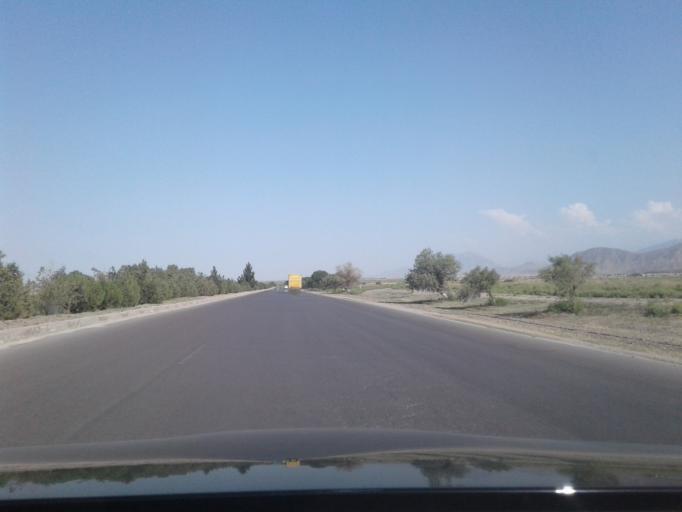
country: TM
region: Ahal
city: Arcabil
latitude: 38.1904
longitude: 57.8445
